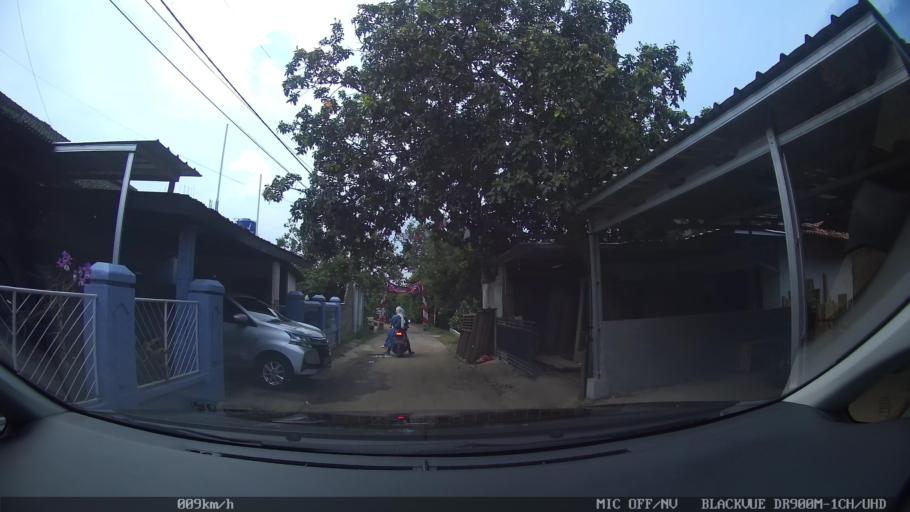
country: ID
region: Lampung
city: Kedaton
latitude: -5.3883
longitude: 105.2127
